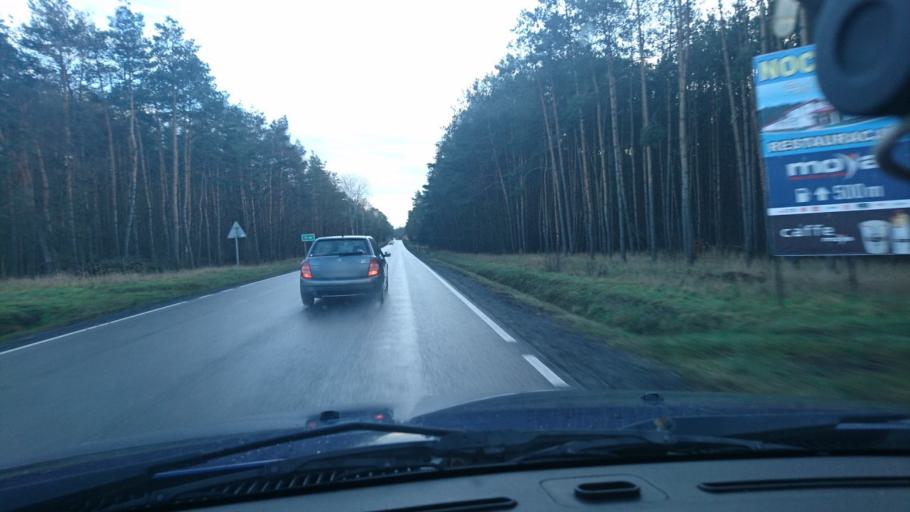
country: PL
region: Greater Poland Voivodeship
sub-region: Powiat kepinski
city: Bralin
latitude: 51.3463
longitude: 17.9507
